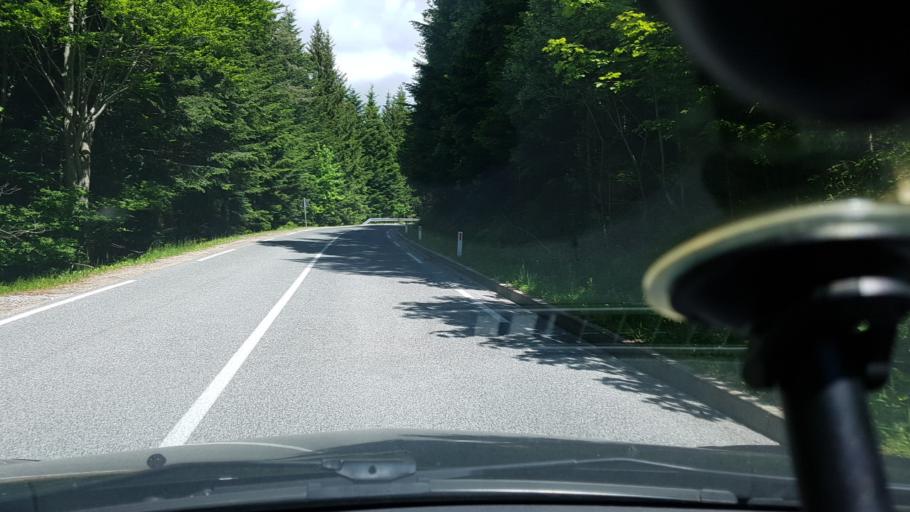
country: SI
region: Zrece
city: Zrece
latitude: 46.4328
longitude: 15.3686
